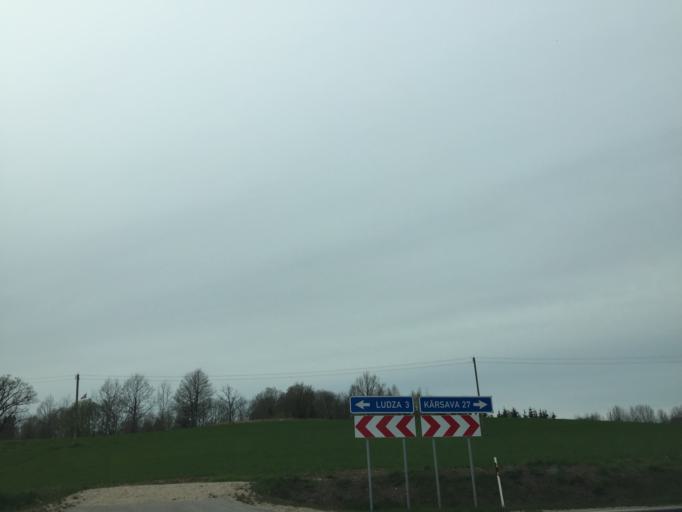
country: LV
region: Ludzas Rajons
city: Ludza
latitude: 56.5669
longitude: 27.7290
